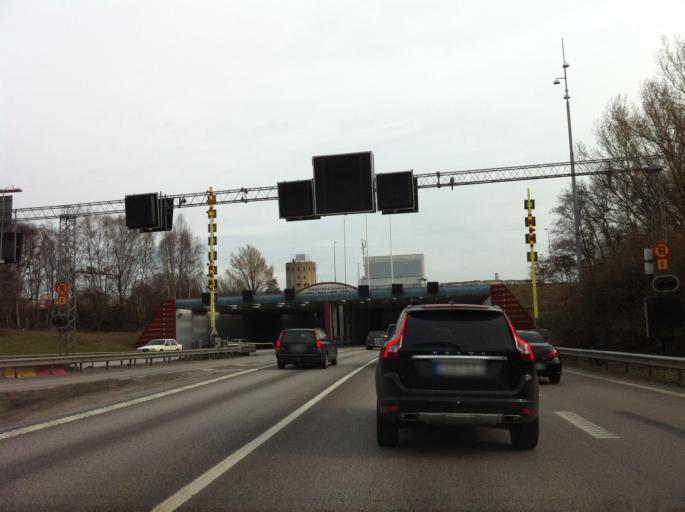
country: SE
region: Vaestra Goetaland
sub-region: Goteborg
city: Hammarkullen
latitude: 57.7806
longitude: 11.9988
